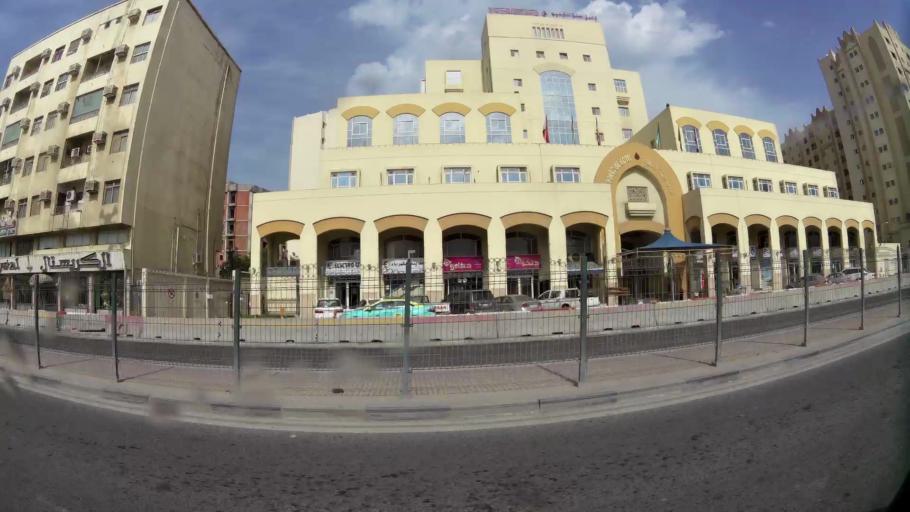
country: QA
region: Baladiyat ad Dawhah
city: Doha
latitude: 25.2819
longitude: 51.5178
